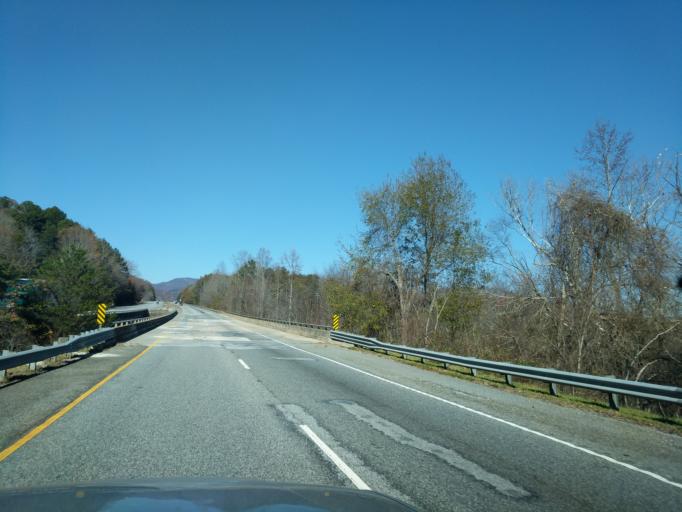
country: US
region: South Carolina
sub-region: Greenville County
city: Slater-Marietta
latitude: 35.1100
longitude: -82.4548
